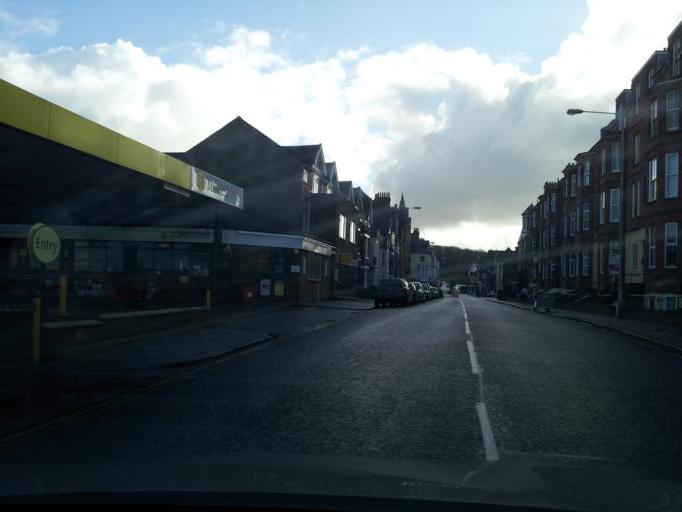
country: GB
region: England
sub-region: Norfolk
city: Cromer
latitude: 52.9326
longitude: 1.2981
